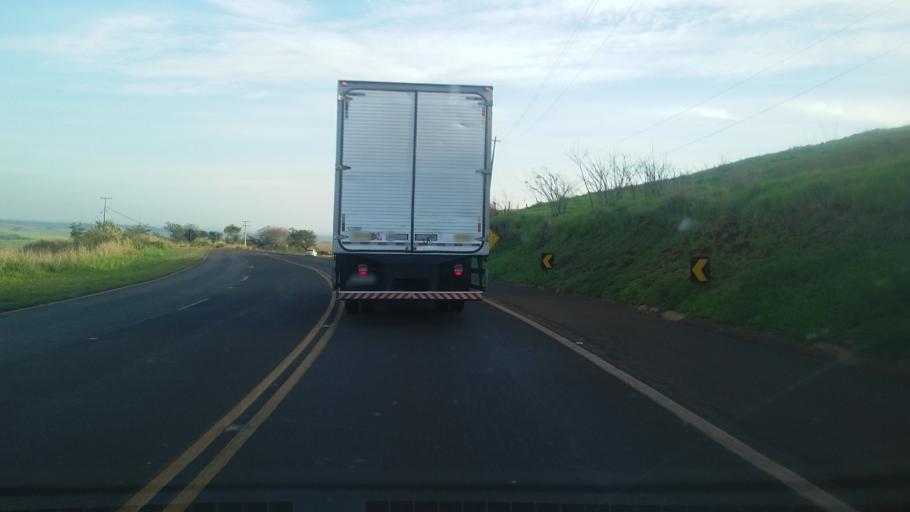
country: BR
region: Parana
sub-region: Bandeirantes
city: Bandeirantes
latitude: -23.1714
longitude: -50.6132
